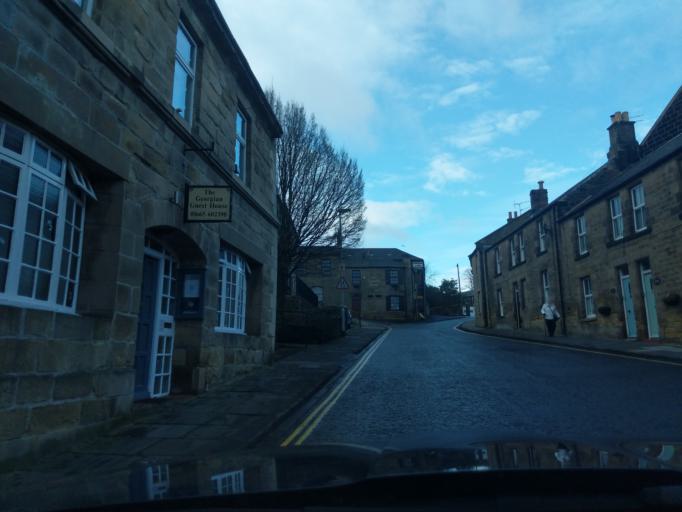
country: GB
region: England
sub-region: Northumberland
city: Alnwick
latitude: 55.4123
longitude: -1.7038
